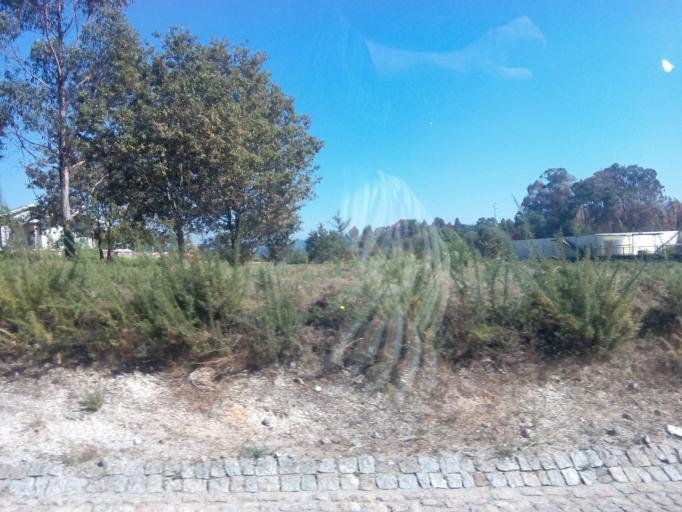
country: PT
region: Porto
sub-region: Paredes
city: Casteloes de Cepeda
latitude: 41.1948
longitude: -8.3451
